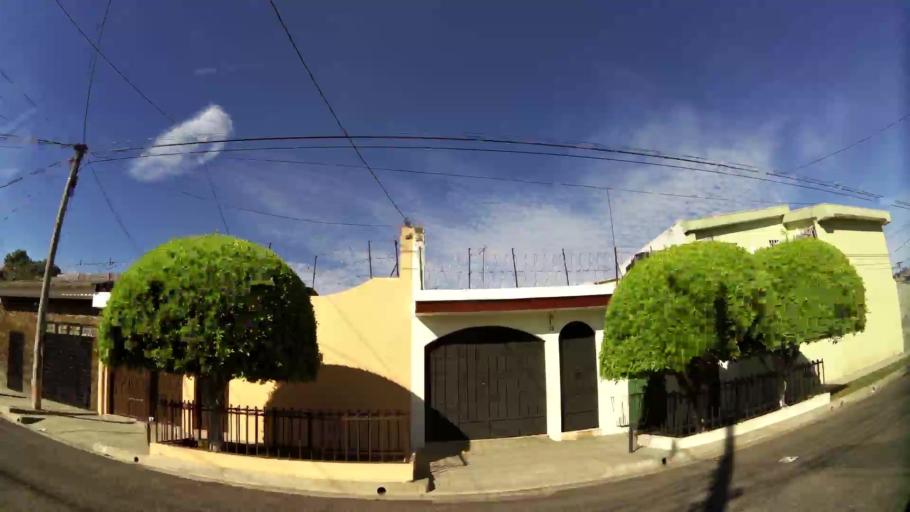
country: SV
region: Santa Ana
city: Santa Ana
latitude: 13.9991
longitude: -89.5617
